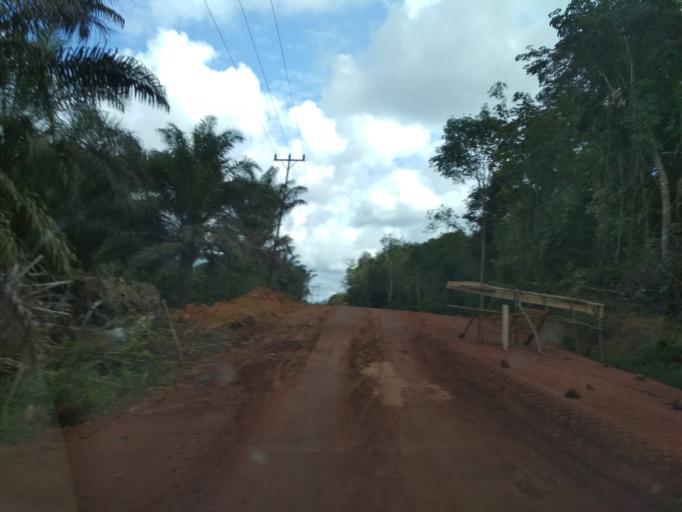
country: ID
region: West Kalimantan
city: Tayan
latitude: 0.5409
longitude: 110.0894
